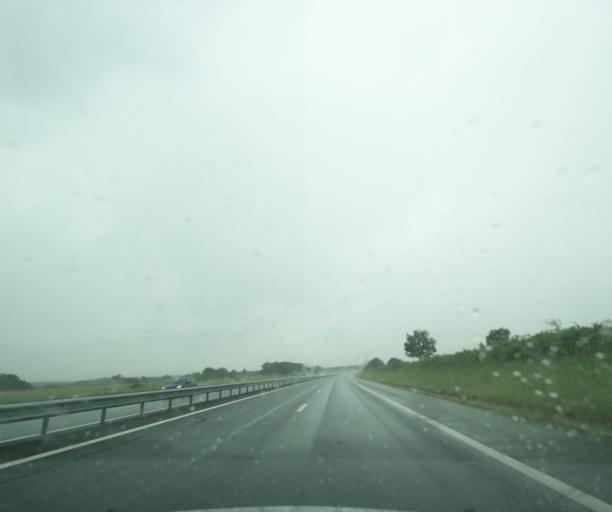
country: FR
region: Auvergne
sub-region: Departement de l'Allier
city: Vallon-en-Sully
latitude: 46.5977
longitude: 2.5120
